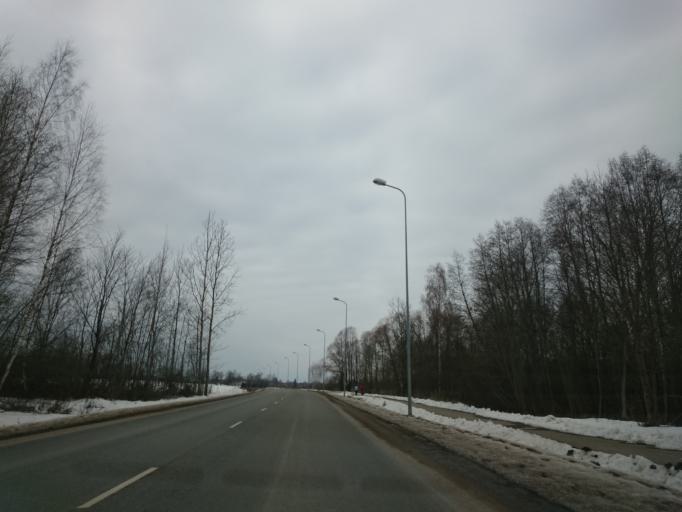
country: LV
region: Cesu Rajons
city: Cesis
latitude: 57.2961
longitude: 25.2583
